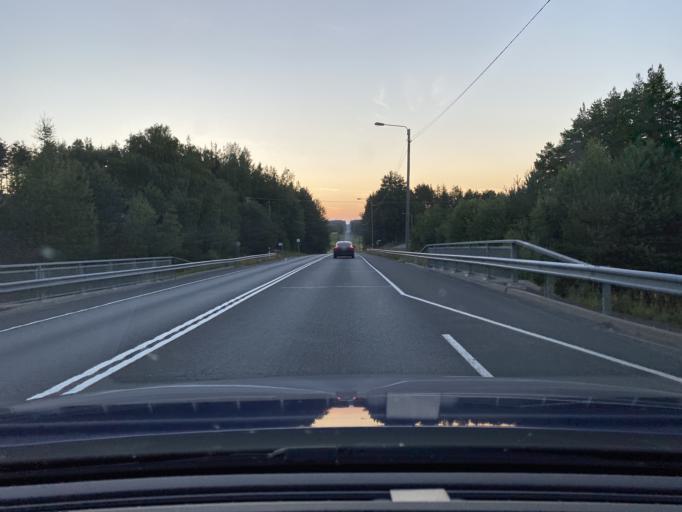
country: FI
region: Pirkanmaa
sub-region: Luoteis-Pirkanmaa
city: Ikaalinen
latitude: 61.7640
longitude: 23.0213
